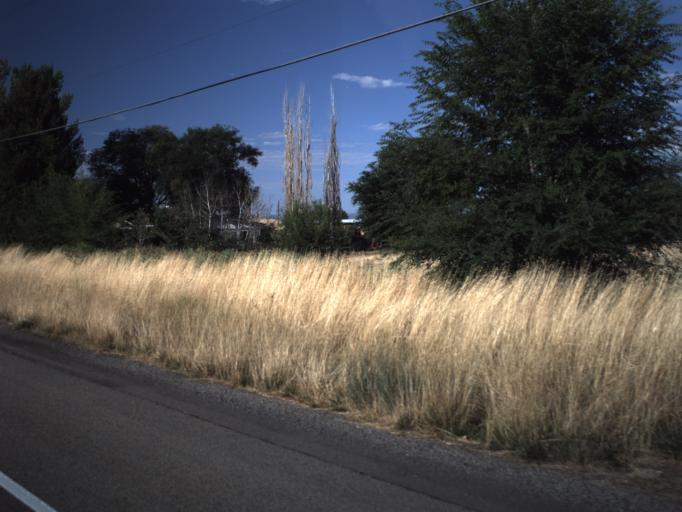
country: US
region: Utah
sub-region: Utah County
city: Salem
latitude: 40.0782
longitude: -111.6597
